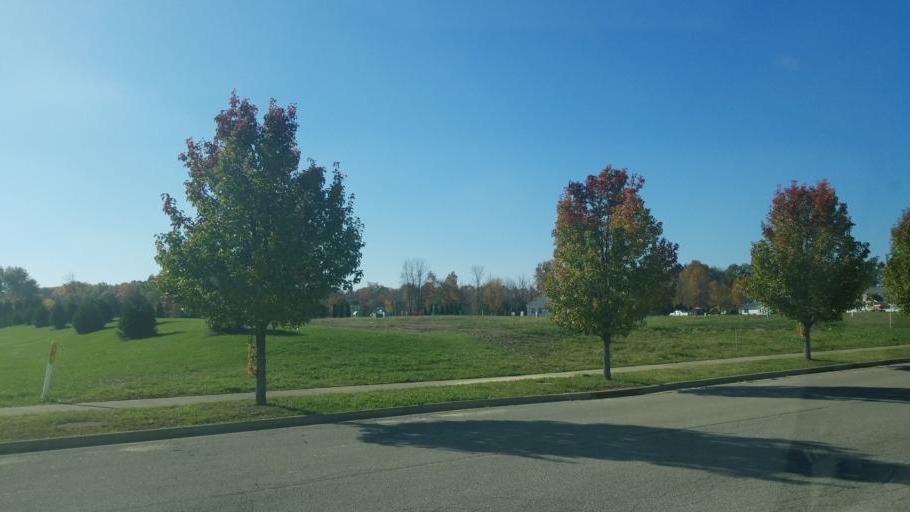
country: US
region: Ohio
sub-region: Ashland County
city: Ashland
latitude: 40.8414
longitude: -82.3358
